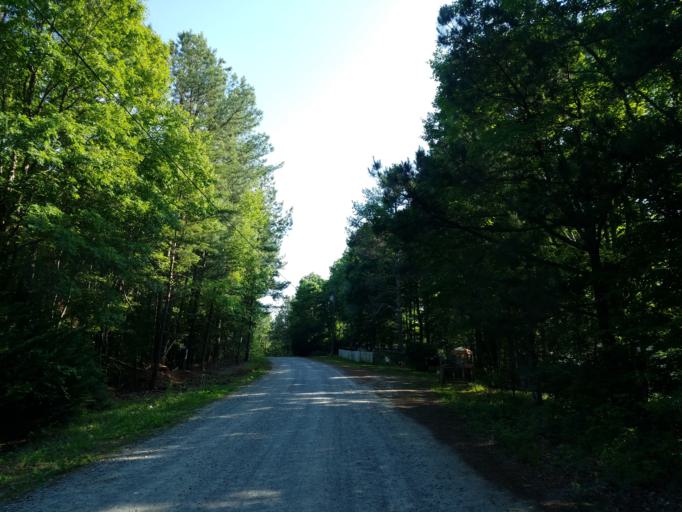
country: US
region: Georgia
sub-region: Pickens County
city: Nelson
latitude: 34.3696
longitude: -84.3411
